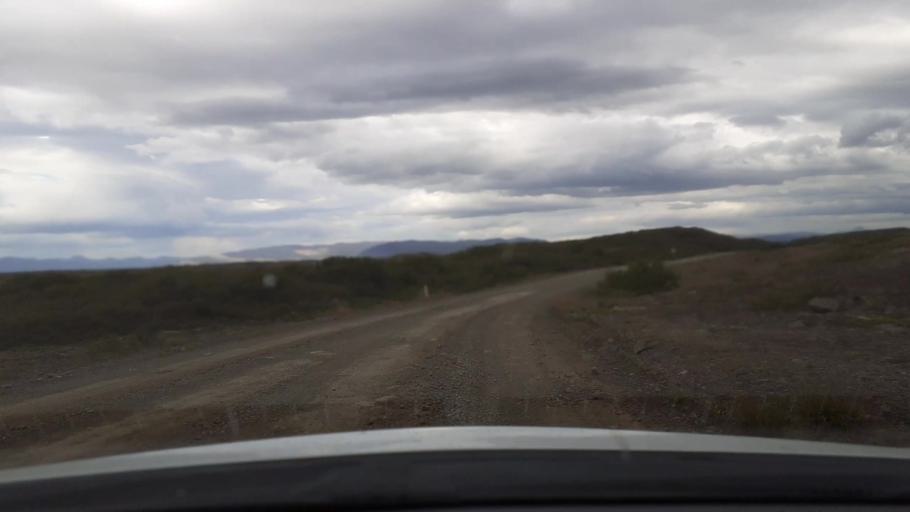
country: IS
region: West
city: Borgarnes
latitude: 64.5935
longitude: -21.9868
